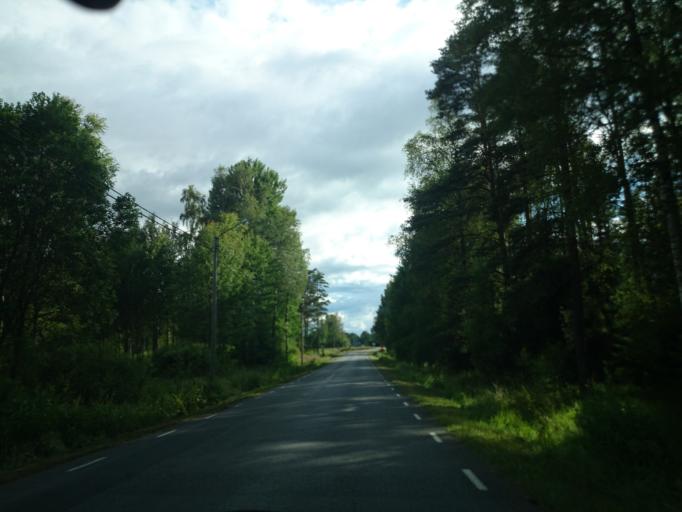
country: SE
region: Joenkoeping
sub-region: Varnamo Kommun
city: Forsheda
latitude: 57.1680
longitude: 13.8383
